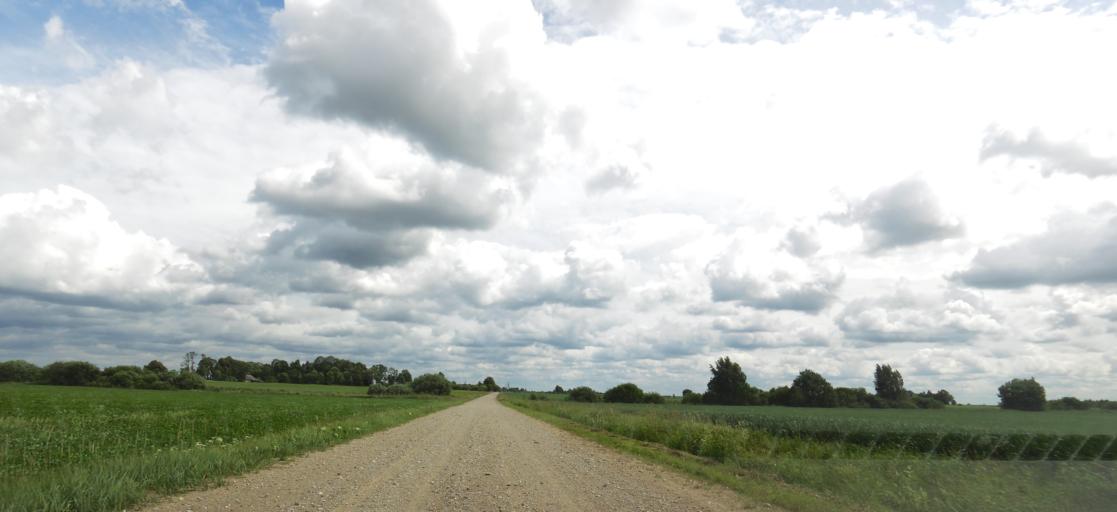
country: LT
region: Panevezys
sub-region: Birzai
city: Birzai
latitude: 56.3159
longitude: 24.7617
